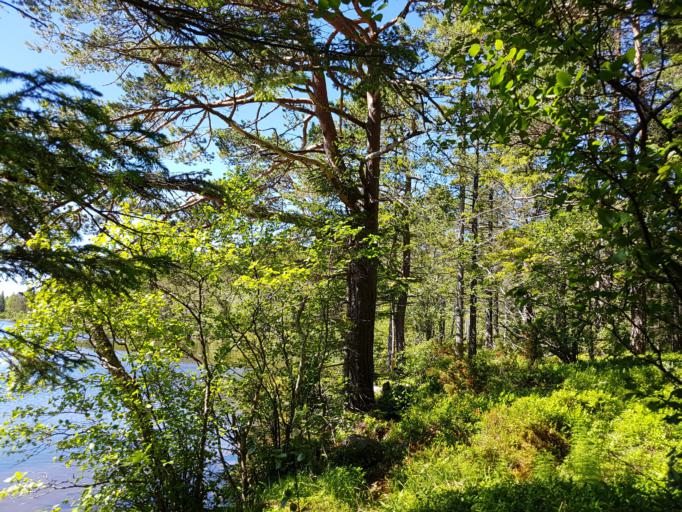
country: NO
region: Sor-Trondelag
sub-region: Melhus
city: Melhus
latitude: 63.4383
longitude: 10.2176
